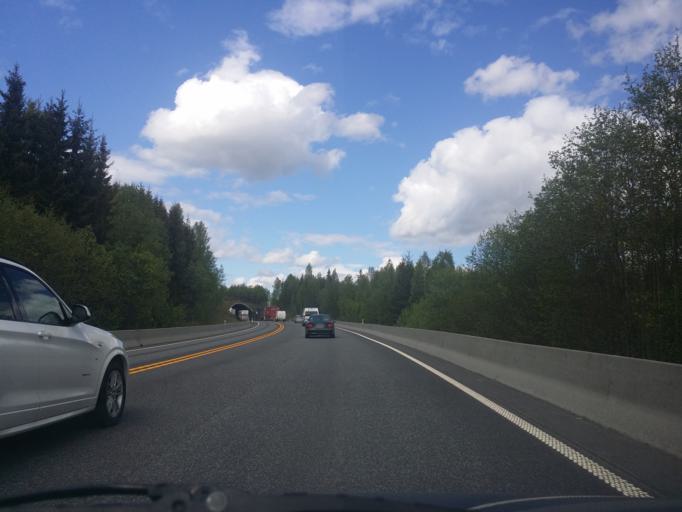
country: NO
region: Oppland
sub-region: Lunner
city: Roa
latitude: 60.2692
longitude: 10.5029
